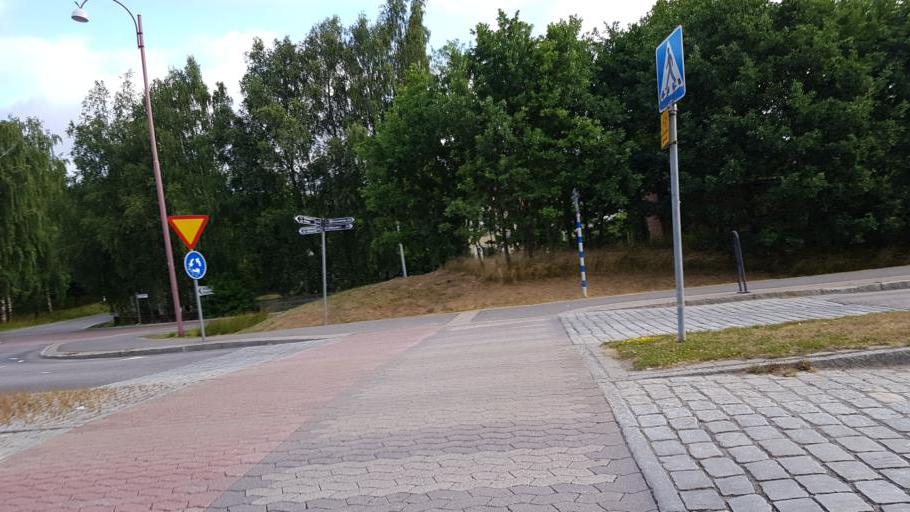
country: SE
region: Vaestra Goetaland
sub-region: Harryda Kommun
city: Molnlycke
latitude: 57.6571
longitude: 12.1087
